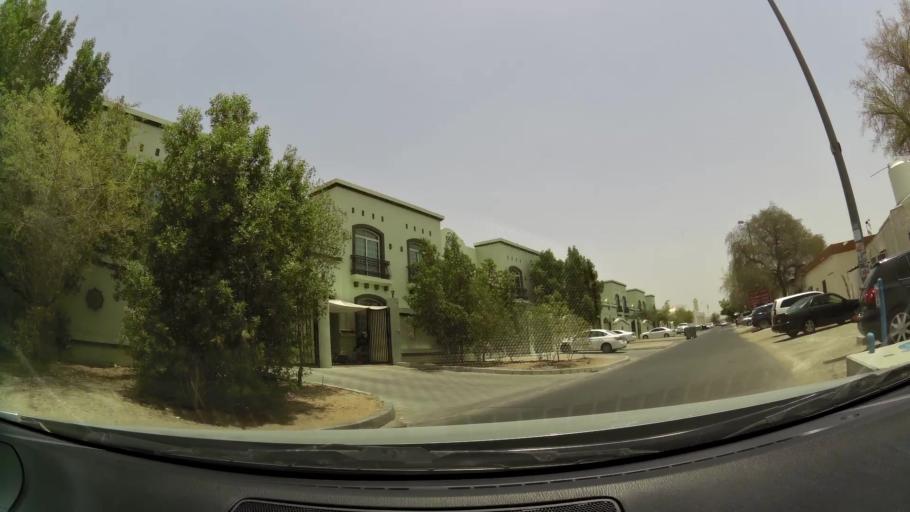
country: AE
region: Abu Dhabi
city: Al Ain
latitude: 24.2121
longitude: 55.7471
